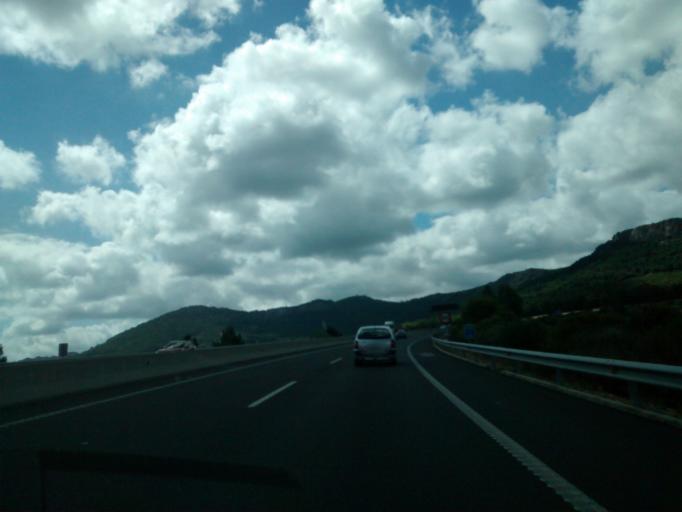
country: ES
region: Extremadura
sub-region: Provincia de Caceres
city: Higuera
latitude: 39.7080
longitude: -5.6910
